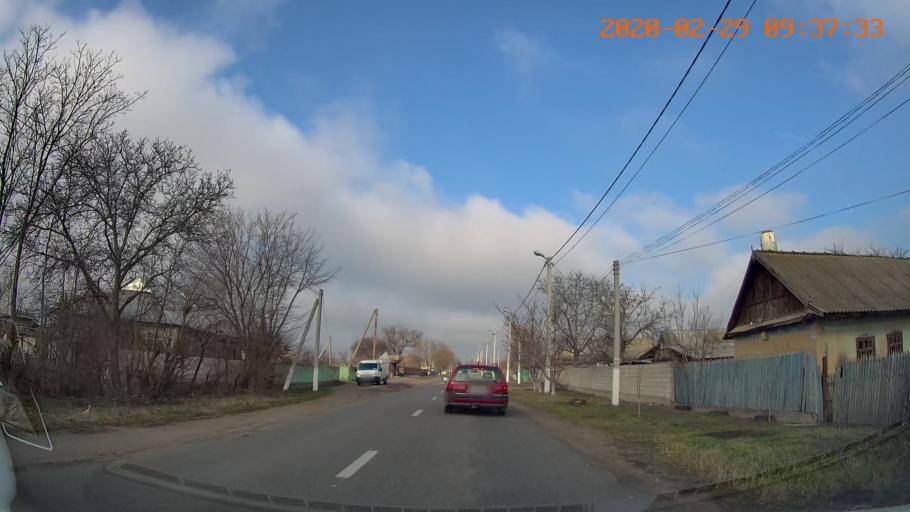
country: MD
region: Telenesti
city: Dnestrovsc
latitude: 46.6282
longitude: 29.8755
